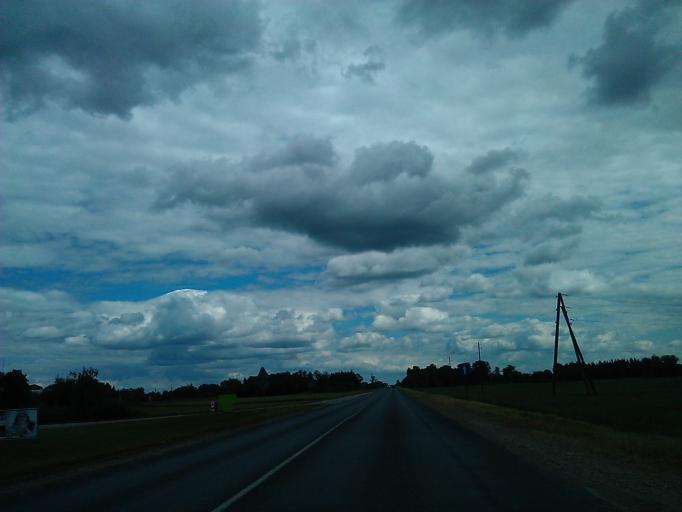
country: LV
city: Tervete
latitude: 56.6220
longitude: 23.4464
